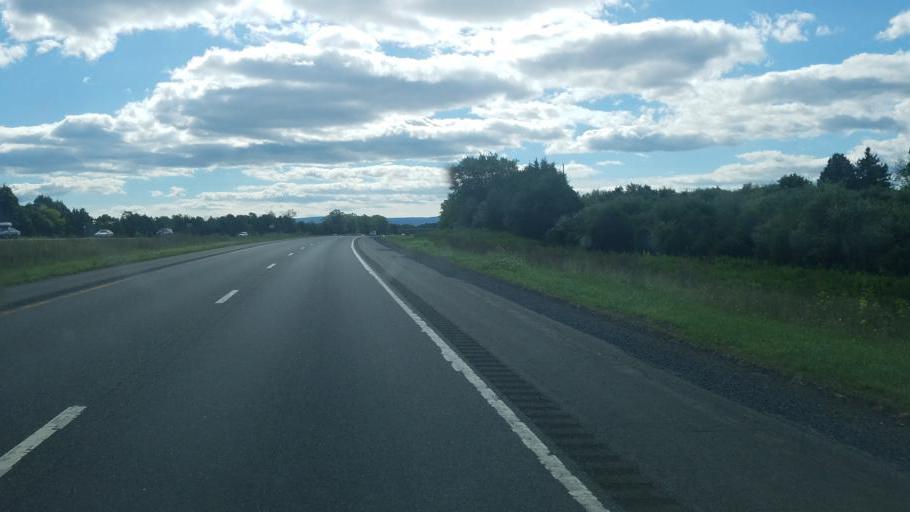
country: US
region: Virginia
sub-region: Frederick County
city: Middletown
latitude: 38.9951
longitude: -78.2571
